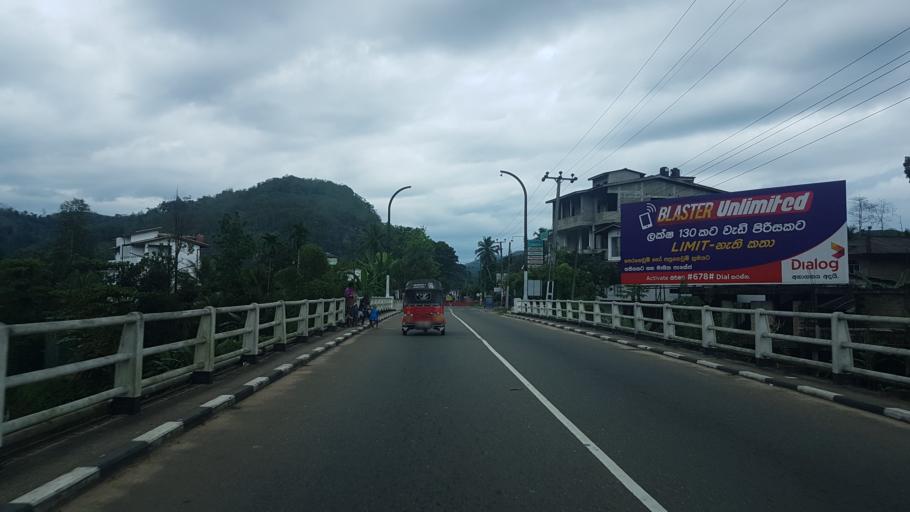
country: LK
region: Western
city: Hanwella Ihala
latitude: 7.0329
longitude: 80.2938
